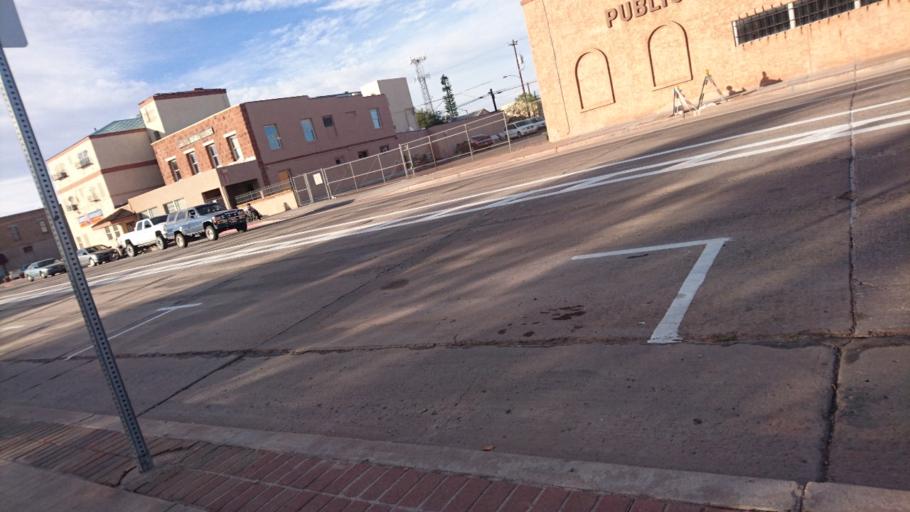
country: US
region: Arizona
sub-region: Navajo County
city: Winslow
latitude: 35.0225
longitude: -110.6961
